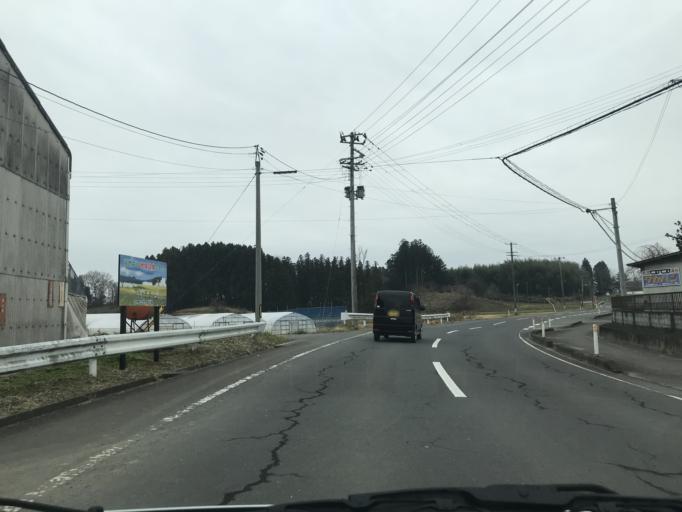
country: JP
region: Miyagi
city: Wakuya
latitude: 38.7298
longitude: 141.2210
